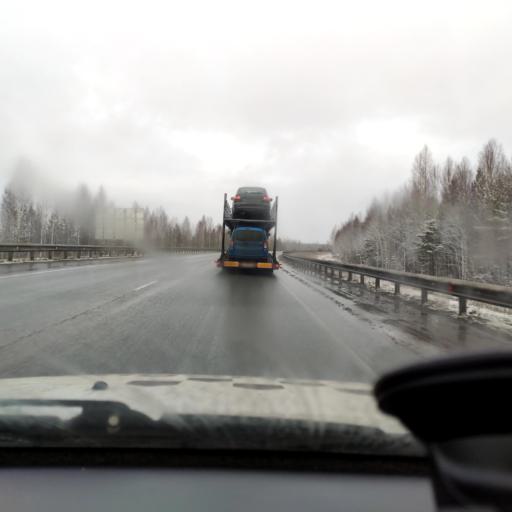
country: RU
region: Perm
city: Krasnokamsk
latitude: 58.0869
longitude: 55.6741
